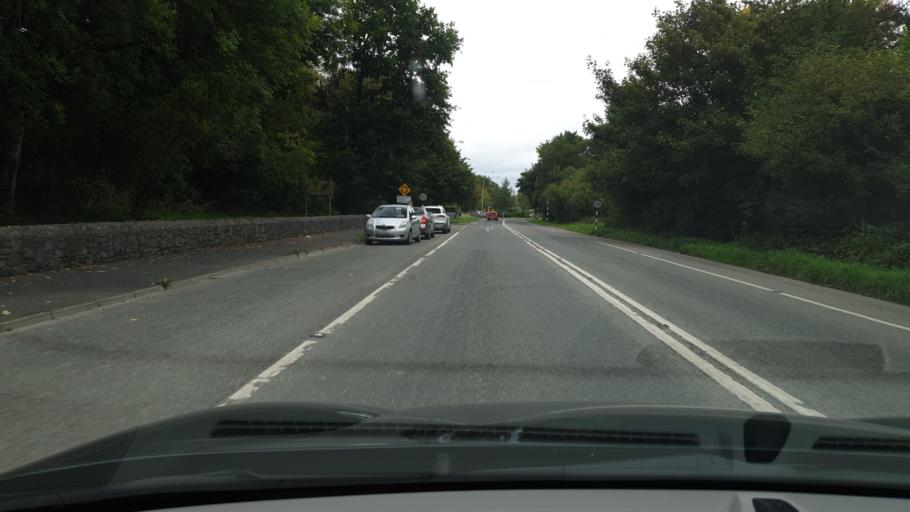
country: IE
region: Leinster
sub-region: Kildare
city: Maynooth
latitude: 53.3817
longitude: -6.6038
